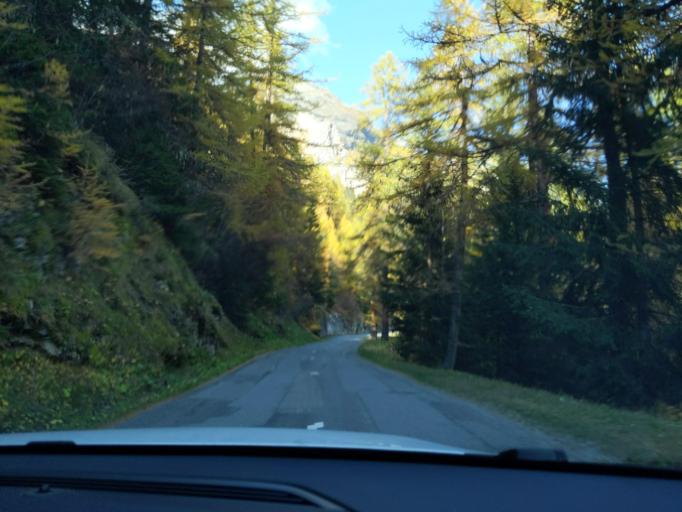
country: FR
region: Rhone-Alpes
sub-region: Departement de la Savoie
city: Tignes
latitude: 45.5014
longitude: 6.9206
